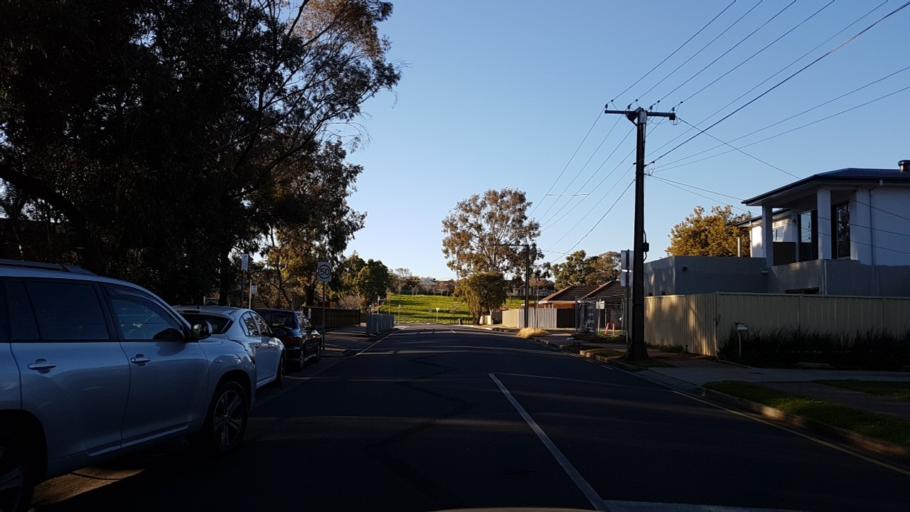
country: AU
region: South Australia
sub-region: Campbelltown
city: Hectorville
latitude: -34.8827
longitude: 138.6545
